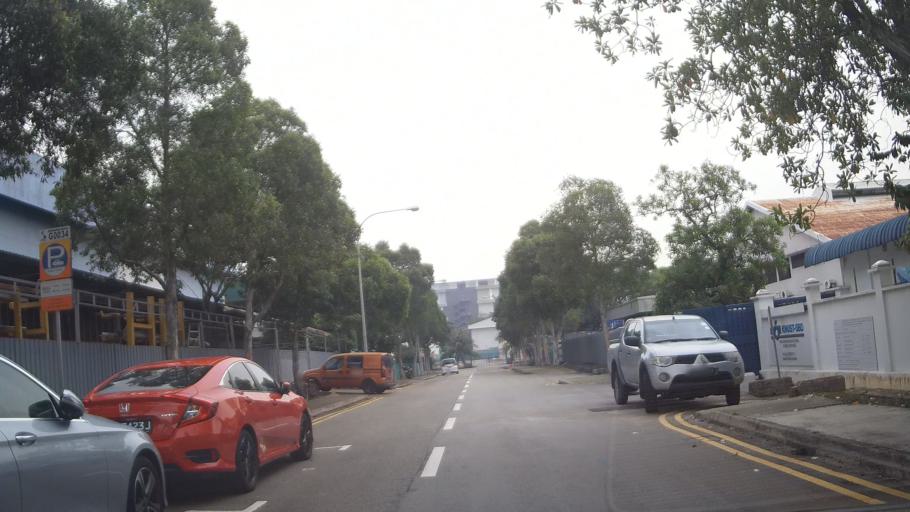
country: MY
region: Johor
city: Johor Bahru
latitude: 1.3182
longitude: 103.6668
